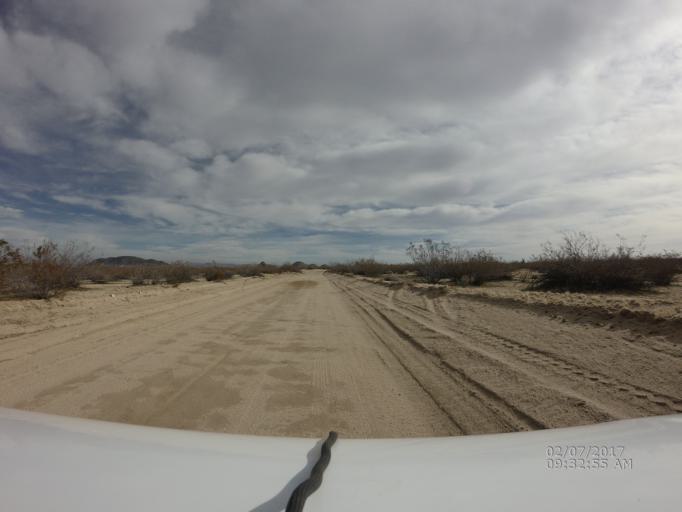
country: US
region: California
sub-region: San Bernardino County
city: Pinon Hills
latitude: 34.5178
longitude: -117.7420
